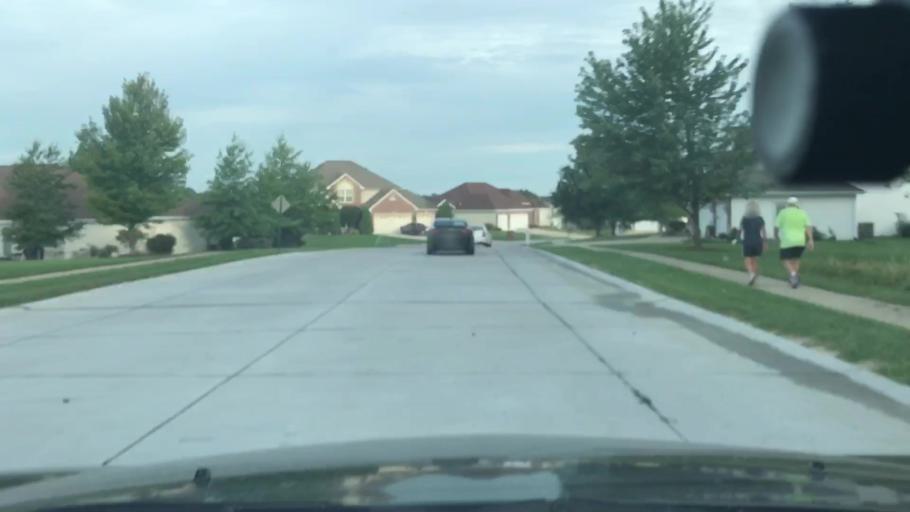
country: US
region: Missouri
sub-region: Saint Charles County
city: Wentzville
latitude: 38.8142
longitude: -90.8890
